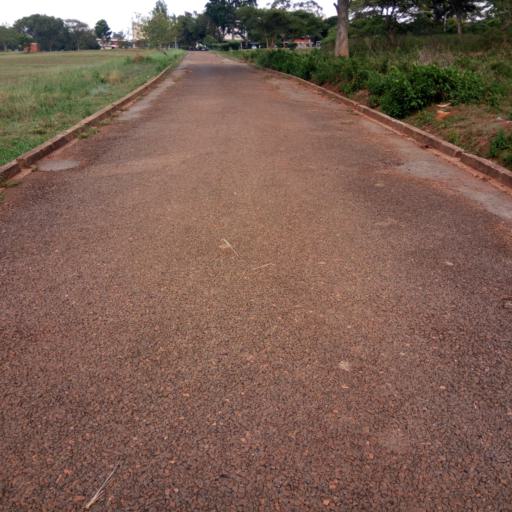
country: UG
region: Eastern Region
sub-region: Busia District
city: Busia
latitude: 0.5451
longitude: 34.0175
